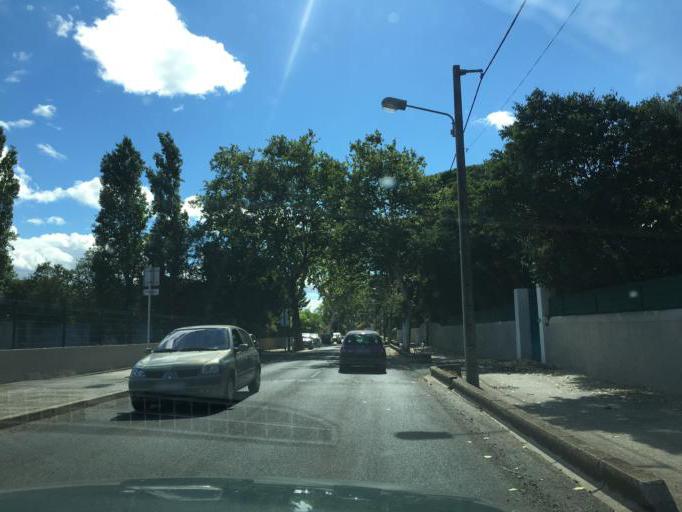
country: FR
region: Languedoc-Roussillon
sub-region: Departement de l'Herault
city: Florensac
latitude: 43.3849
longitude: 3.4716
